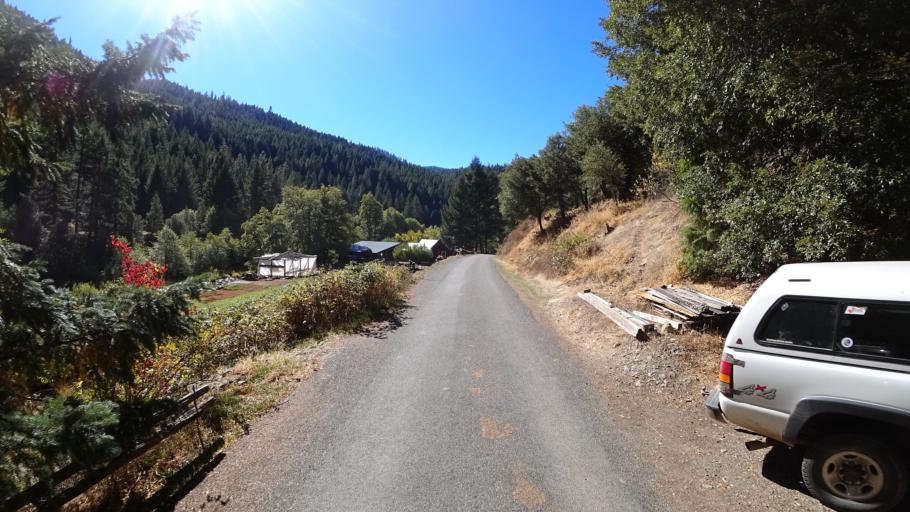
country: US
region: California
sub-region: Siskiyou County
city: Happy Camp
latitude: 41.2975
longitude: -123.1272
